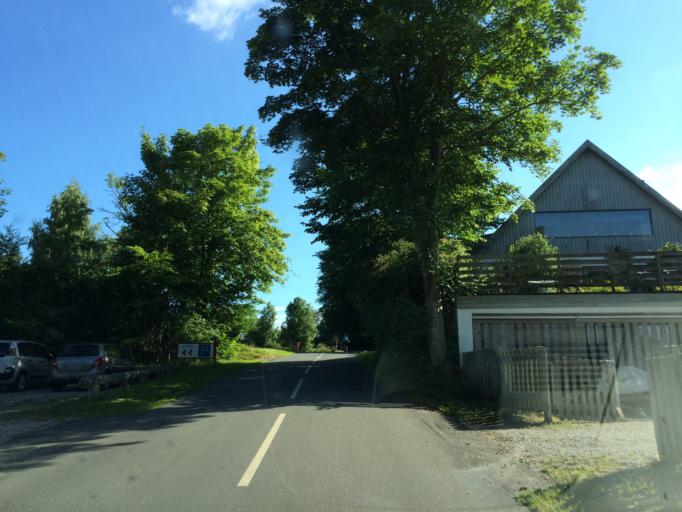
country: DK
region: Central Jutland
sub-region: Syddjurs Kommune
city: Ebeltoft
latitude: 56.2408
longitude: 10.6157
